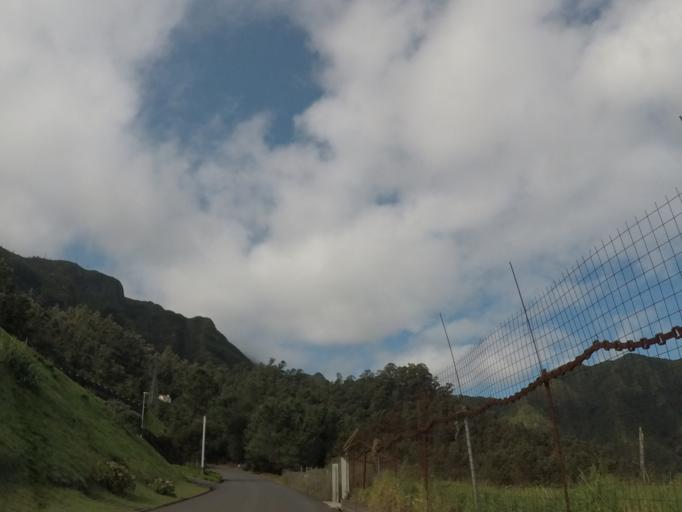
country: PT
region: Madeira
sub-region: Sao Vicente
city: Sao Vicente
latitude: 32.7801
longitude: -17.0458
